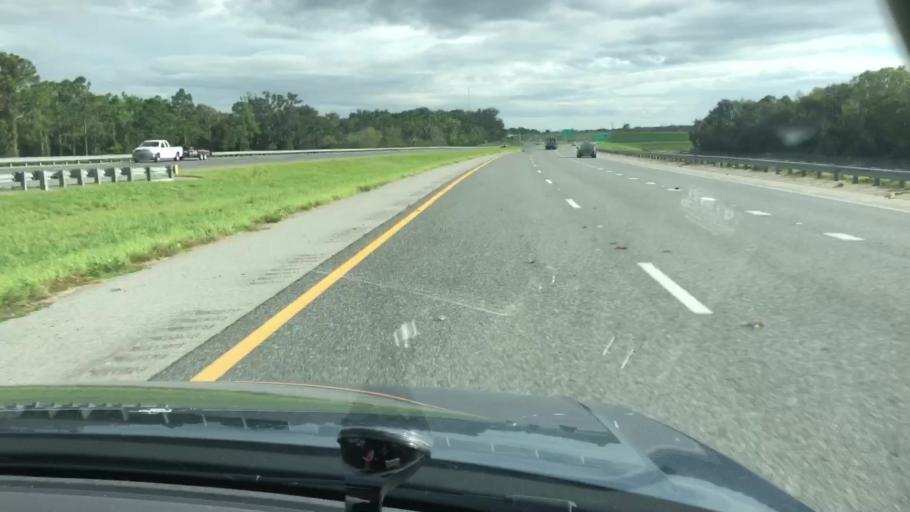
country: US
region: Florida
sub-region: Orange County
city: Apopka
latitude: 28.6684
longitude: -81.5552
